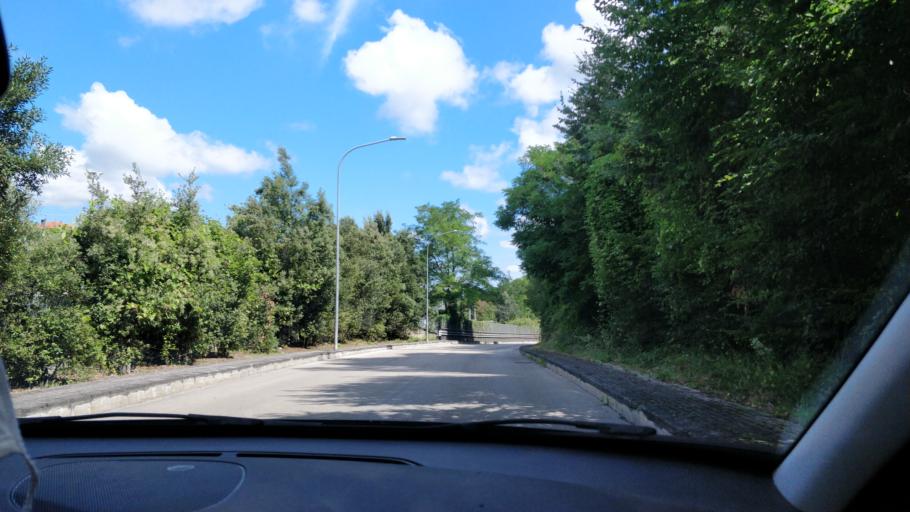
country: IT
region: Abruzzo
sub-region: Provincia di Chieti
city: Lanciano
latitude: 42.2282
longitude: 14.4028
